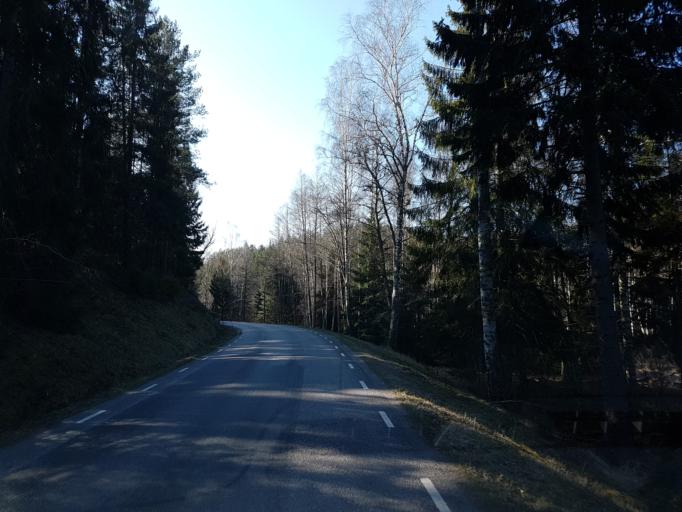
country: SE
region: Kalmar
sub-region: Vasterviks Kommun
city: Overum
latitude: 58.1843
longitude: 16.2803
